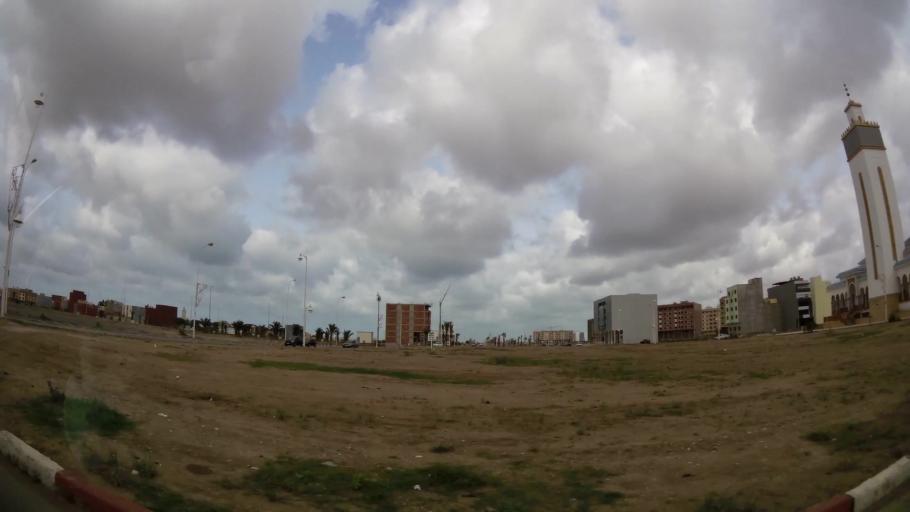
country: MA
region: Oriental
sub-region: Nador
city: Nador
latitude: 35.1532
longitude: -2.9194
